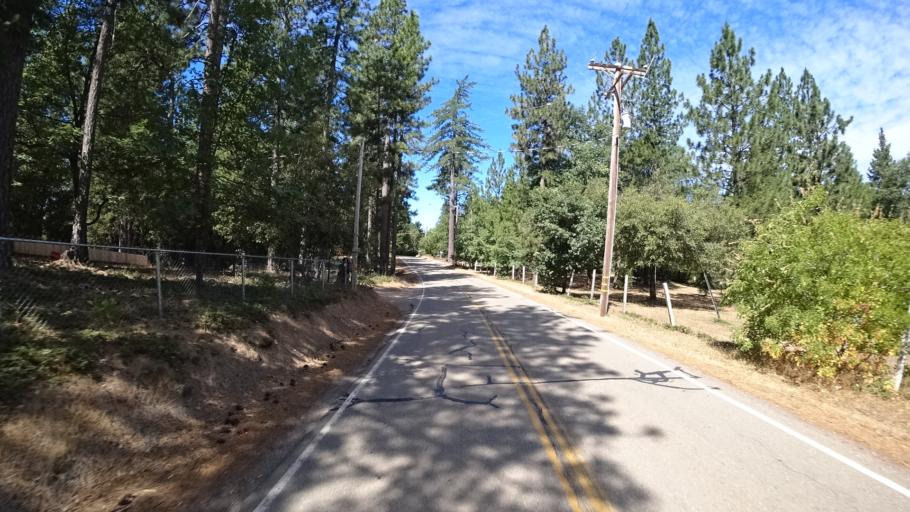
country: US
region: California
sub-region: Amador County
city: Pioneer
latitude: 38.3361
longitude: -120.5304
